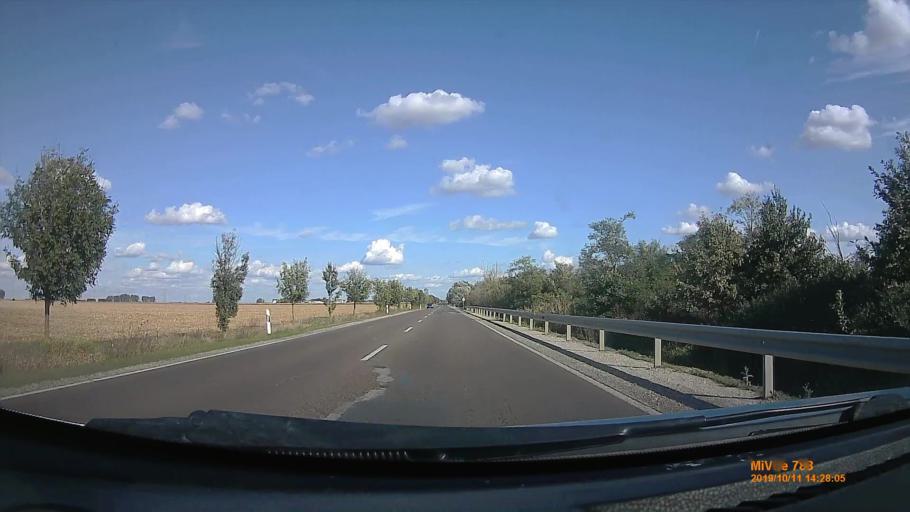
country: HU
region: Hajdu-Bihar
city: Balmazujvaros
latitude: 47.5564
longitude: 21.3618
